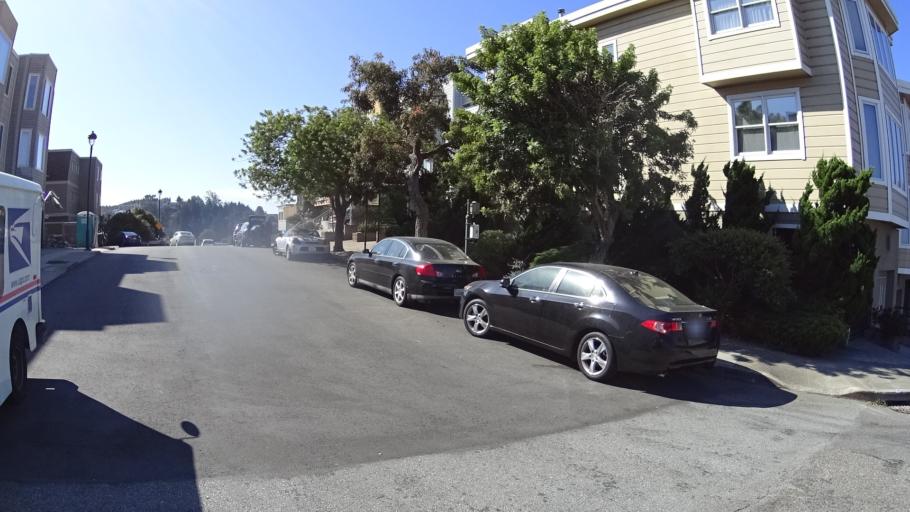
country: US
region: California
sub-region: San Francisco County
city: San Francisco
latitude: 37.7456
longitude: -122.4335
